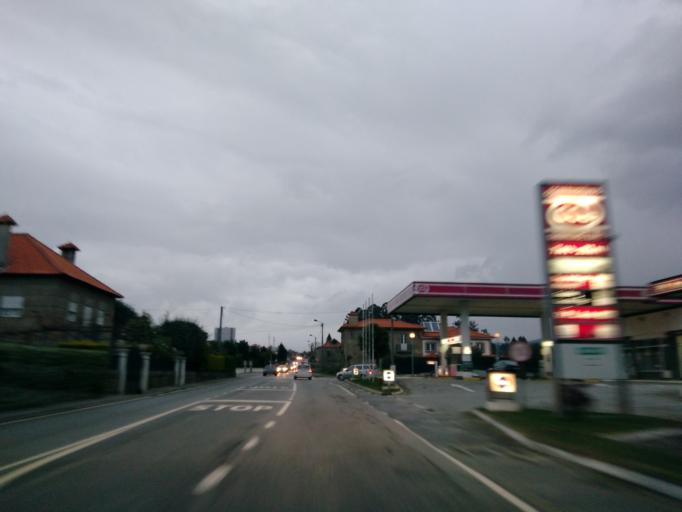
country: PT
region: Braga
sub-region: Braga
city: Oliveira
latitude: 41.4716
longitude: -8.4877
